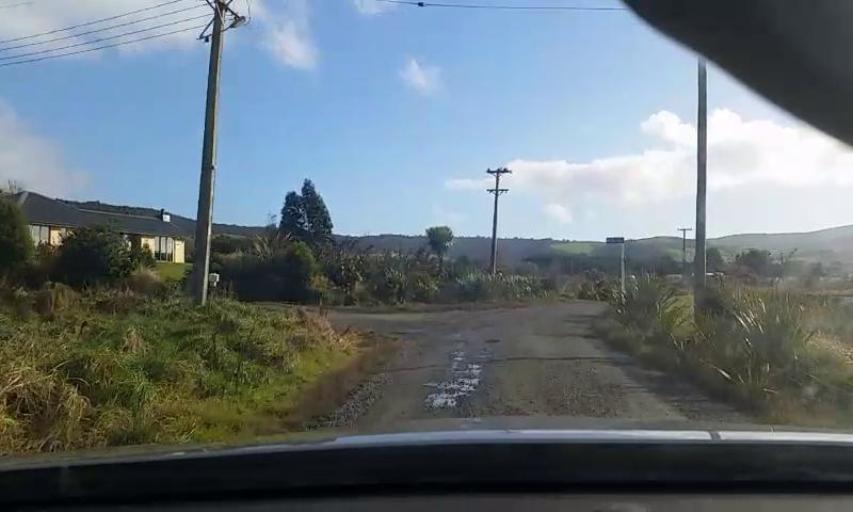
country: NZ
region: Otago
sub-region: Clutha District
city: Papatowai
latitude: -46.6282
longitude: 169.1370
